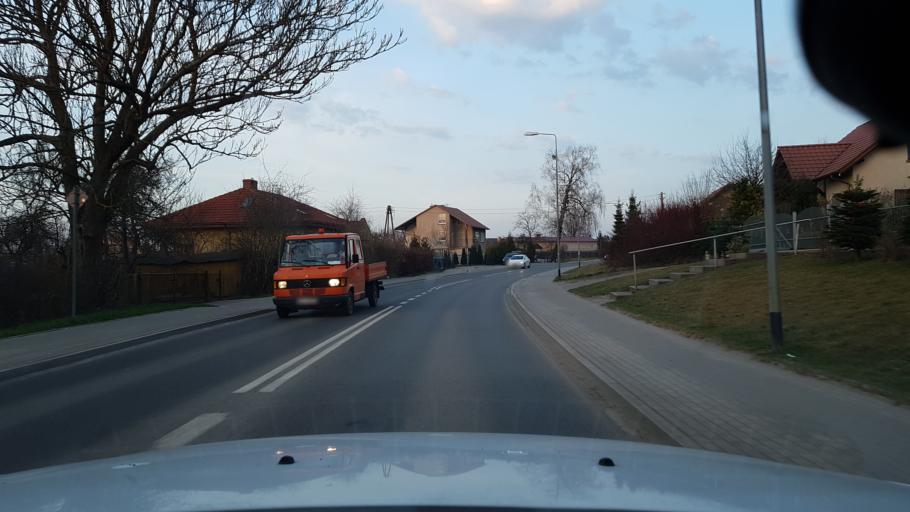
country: PL
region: West Pomeranian Voivodeship
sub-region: Koszalin
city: Koszalin
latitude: 54.1546
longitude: 16.2071
